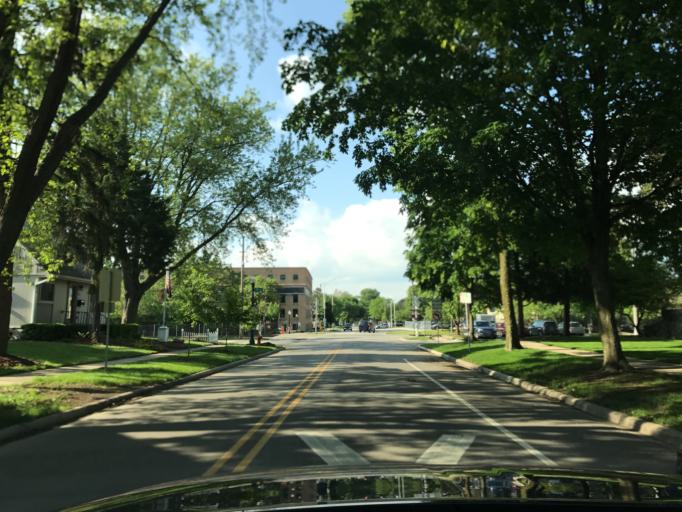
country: US
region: Illinois
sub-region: DuPage County
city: Naperville
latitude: 41.7790
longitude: -88.1422
